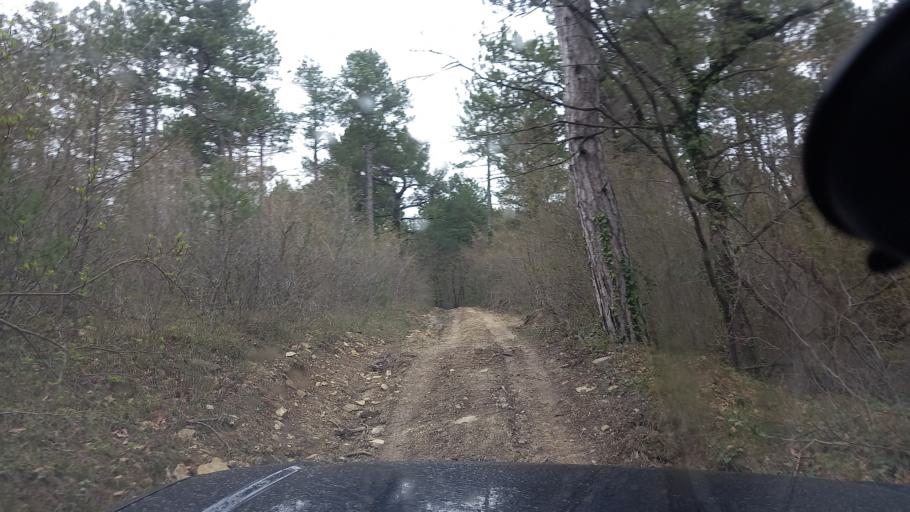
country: RU
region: Krasnodarskiy
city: Arkhipo-Osipovka
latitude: 44.3737
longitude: 38.4732
